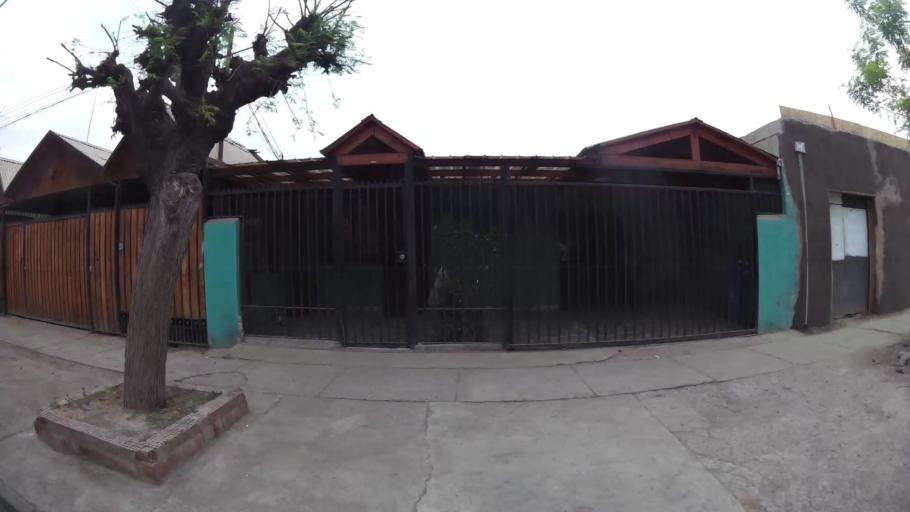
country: CL
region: Santiago Metropolitan
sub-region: Provincia de Chacabuco
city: Chicureo Abajo
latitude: -33.1962
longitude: -70.6753
